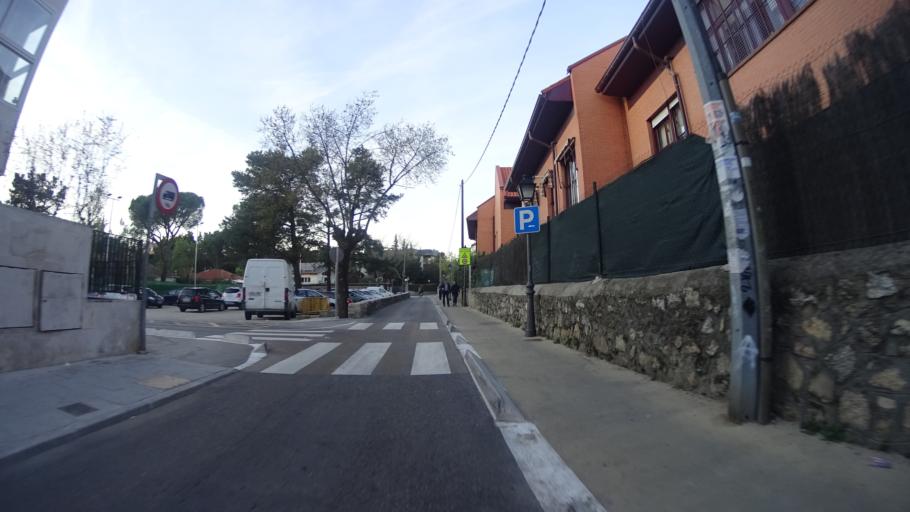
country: ES
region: Madrid
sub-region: Provincia de Madrid
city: Torrelodones
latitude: 40.5756
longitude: -3.9270
